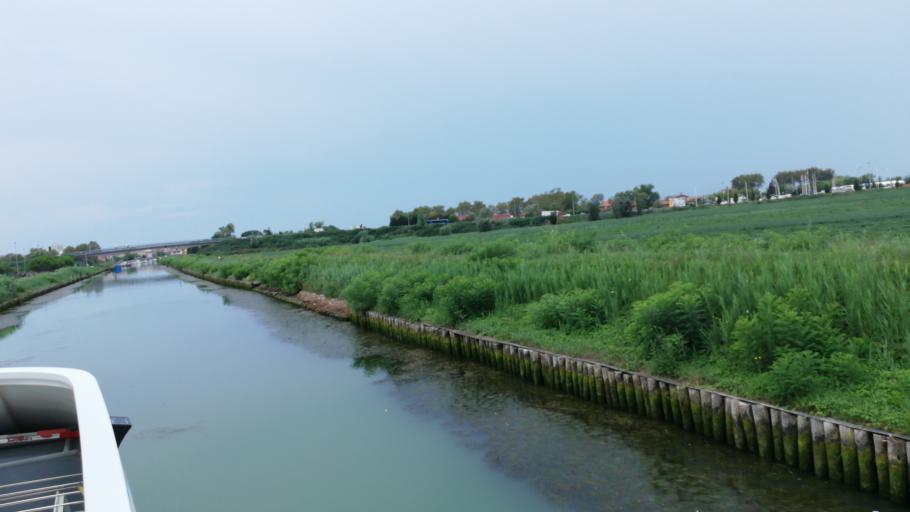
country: IT
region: Veneto
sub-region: Provincia di Venezia
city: Caorle
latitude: 45.6099
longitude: 12.8805
